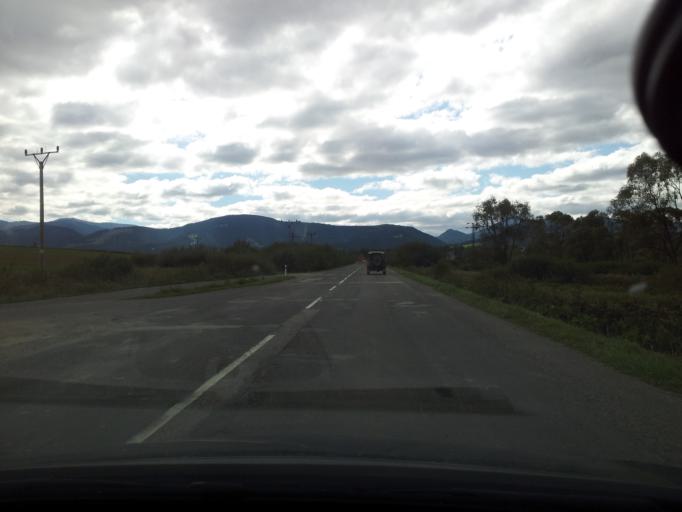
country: SK
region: Zilinsky
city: Ruzomberok
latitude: 49.0822
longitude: 19.4394
